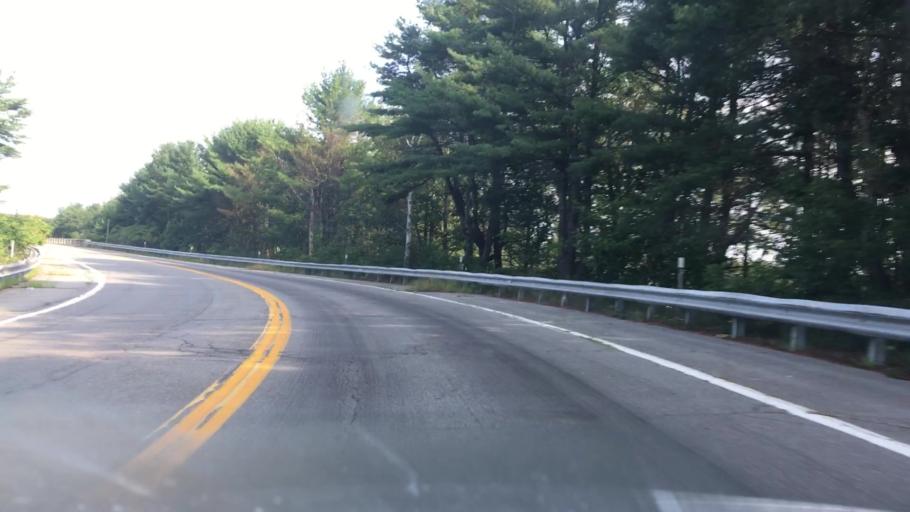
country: US
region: Maine
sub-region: Cumberland County
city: Falmouth
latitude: 43.7294
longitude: -70.2277
